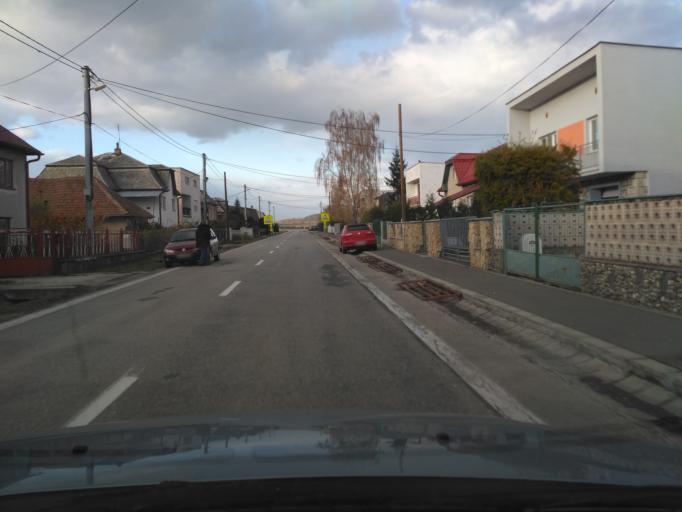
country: HU
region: Borsod-Abauj-Zemplen
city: Satoraljaujhely
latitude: 48.4095
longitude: 21.6680
